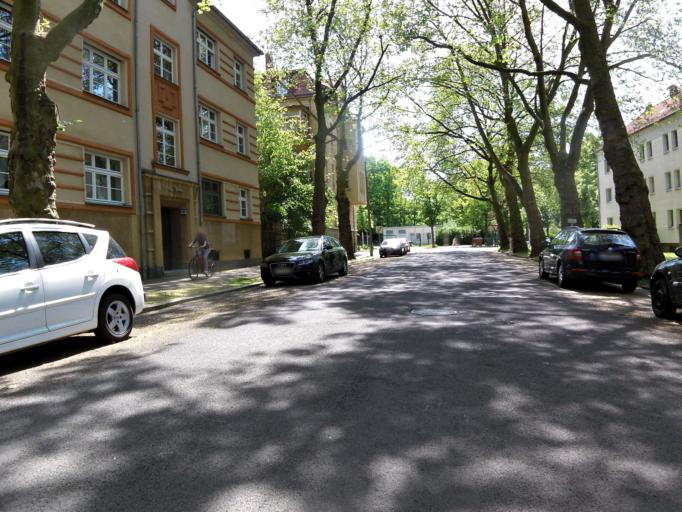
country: DE
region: Saxony
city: Leipzig
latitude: 51.3161
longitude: 12.4199
